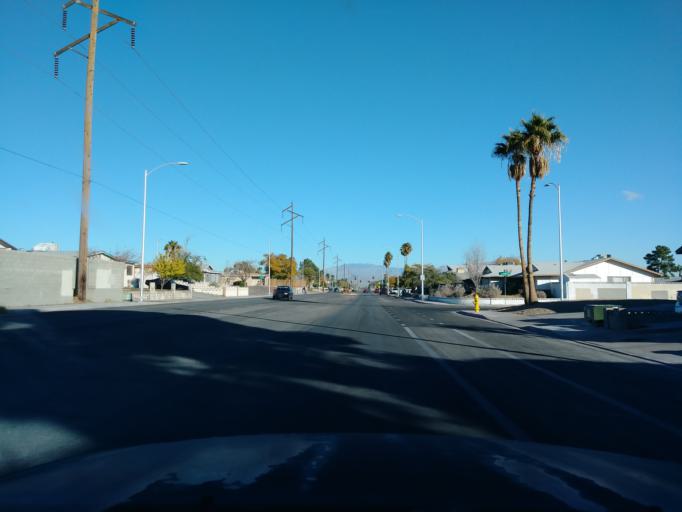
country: US
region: Nevada
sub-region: Clark County
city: Spring Valley
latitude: 36.1638
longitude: -115.2508
